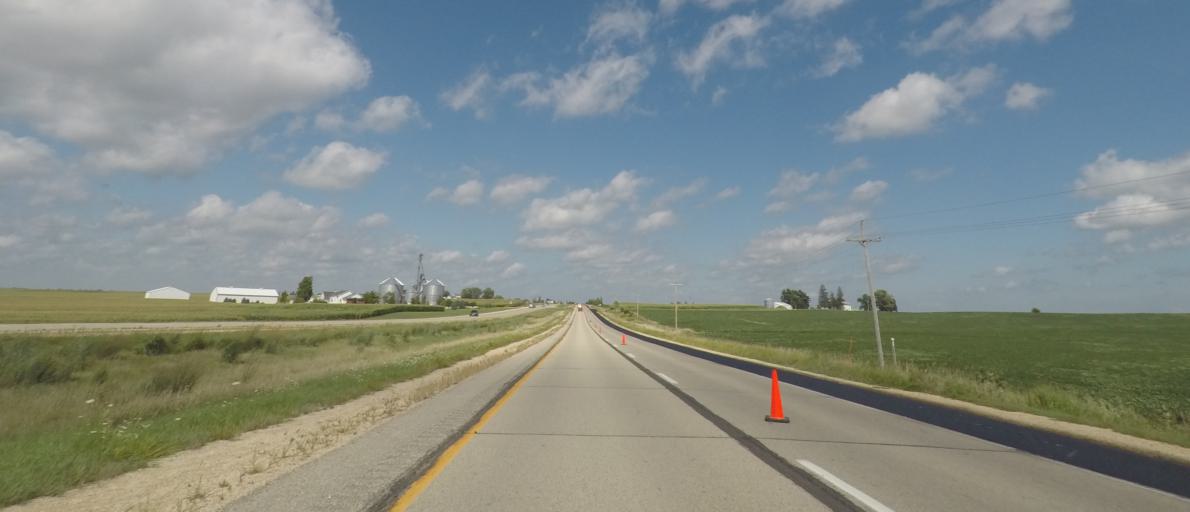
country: US
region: Iowa
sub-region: Jones County
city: Anamosa
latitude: 42.1580
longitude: -91.2356
